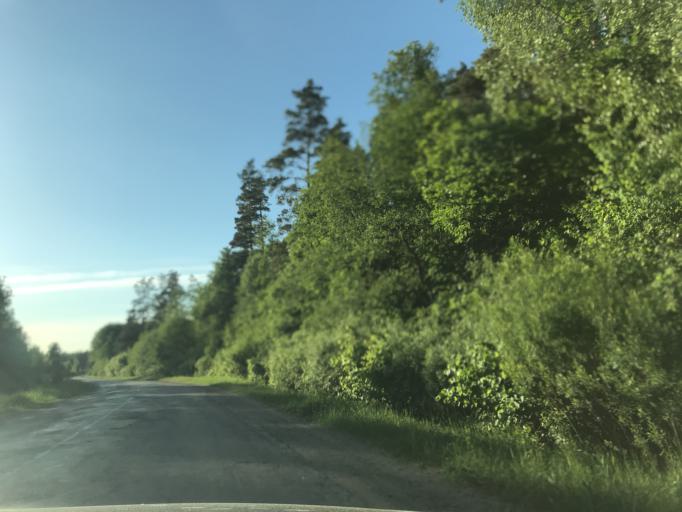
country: LV
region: Ozolnieku
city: Ozolnieki
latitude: 56.6013
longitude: 23.7988
